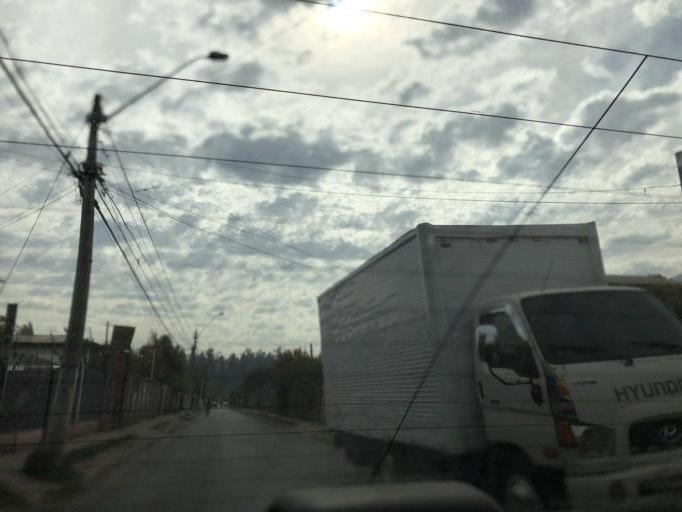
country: CL
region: Santiago Metropolitan
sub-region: Provincia de Cordillera
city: Puente Alto
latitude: -33.6093
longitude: -70.5215
